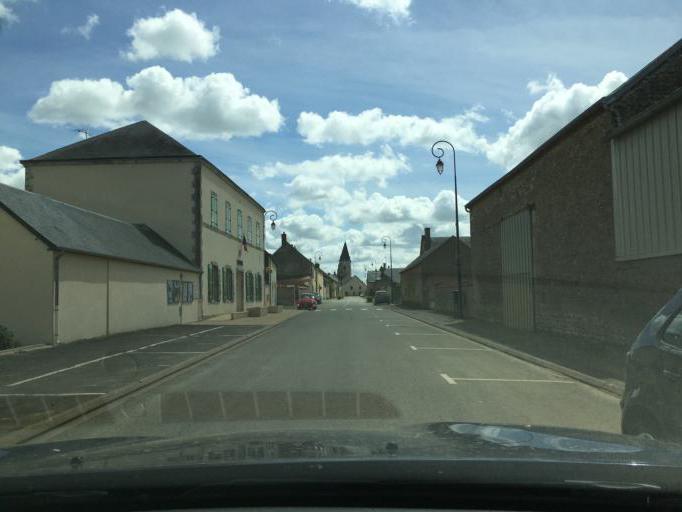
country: FR
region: Centre
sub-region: Departement du Loiret
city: Patay
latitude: 48.0844
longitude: 1.7384
